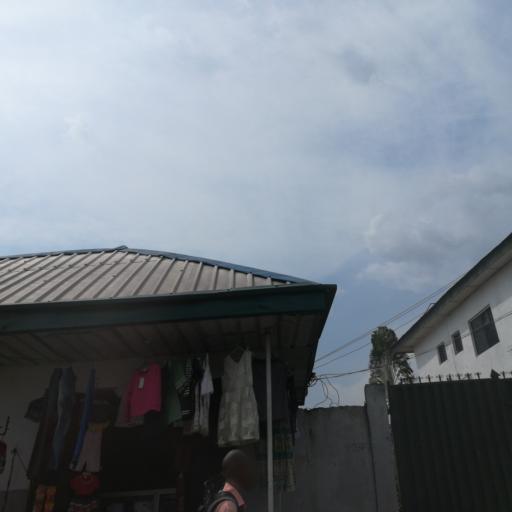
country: NG
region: Rivers
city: Port Harcourt
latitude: 4.8697
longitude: 7.0222
